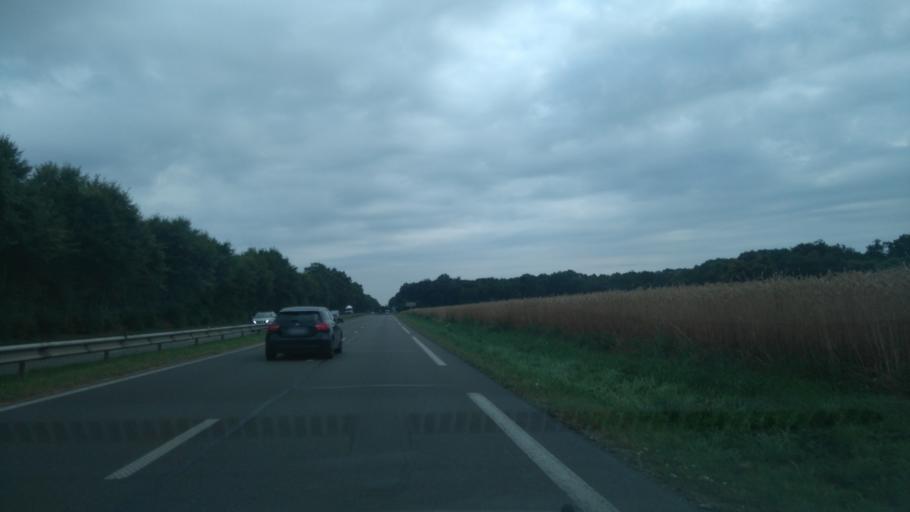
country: FR
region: Picardie
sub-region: Departement de l'Oise
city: Saint-Maximin
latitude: 49.2147
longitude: 2.4652
